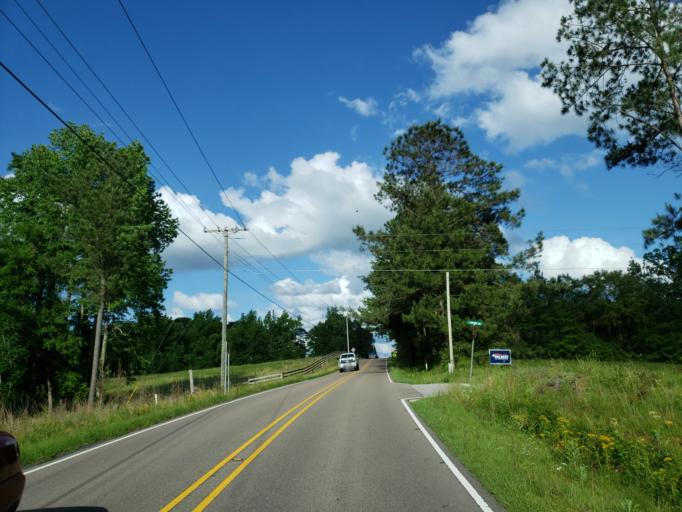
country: US
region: Mississippi
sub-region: Lamar County
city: West Hattiesburg
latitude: 31.2737
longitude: -89.3934
